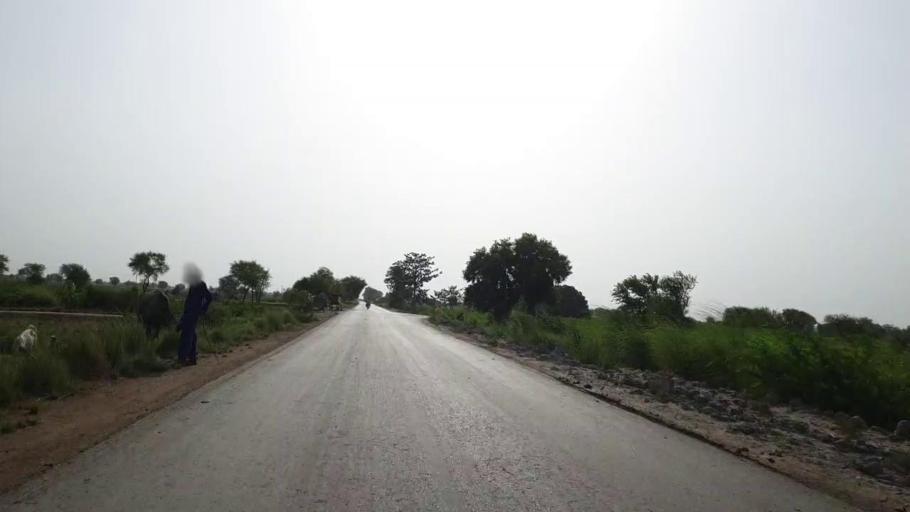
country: PK
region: Sindh
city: Nawabshah
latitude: 26.2599
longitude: 68.4839
